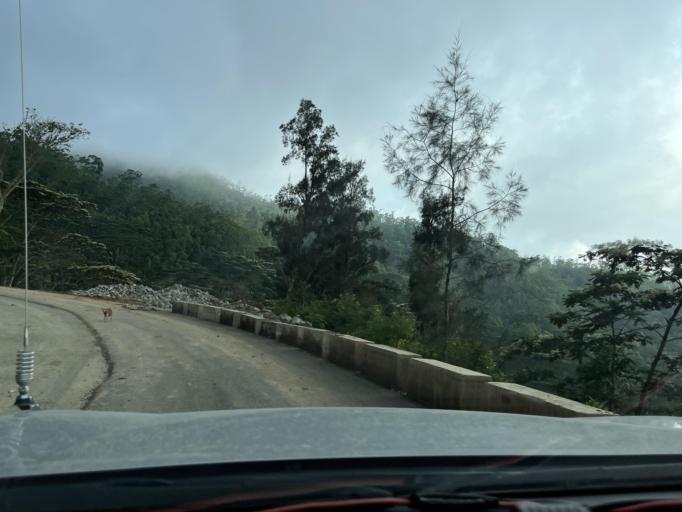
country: TL
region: Aileu
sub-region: Aileu Villa
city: Aileu
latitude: -8.6447
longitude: 125.5872
